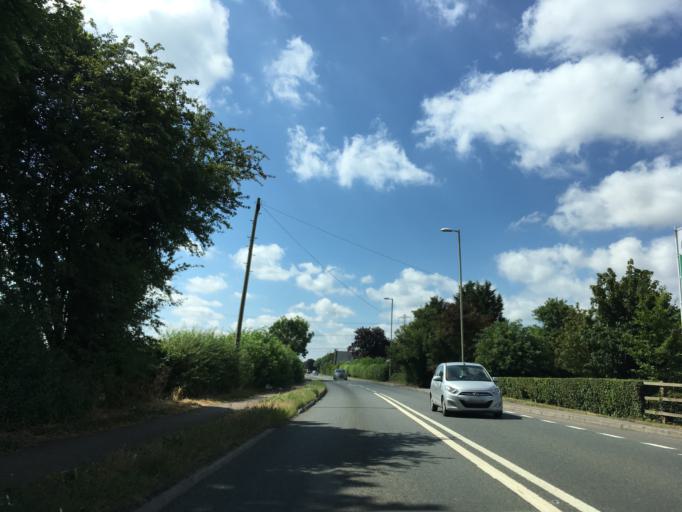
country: GB
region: England
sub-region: Gloucestershire
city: Gloucester
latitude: 51.8931
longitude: -2.2317
